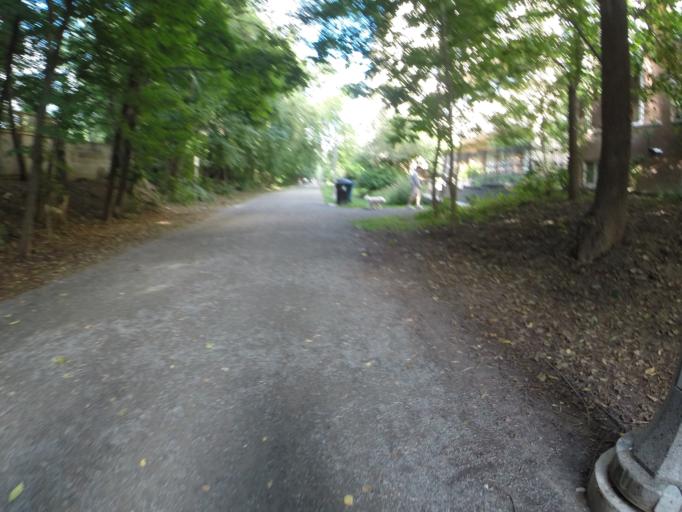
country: CA
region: Ontario
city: Toronto
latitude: 43.6968
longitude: -79.3907
